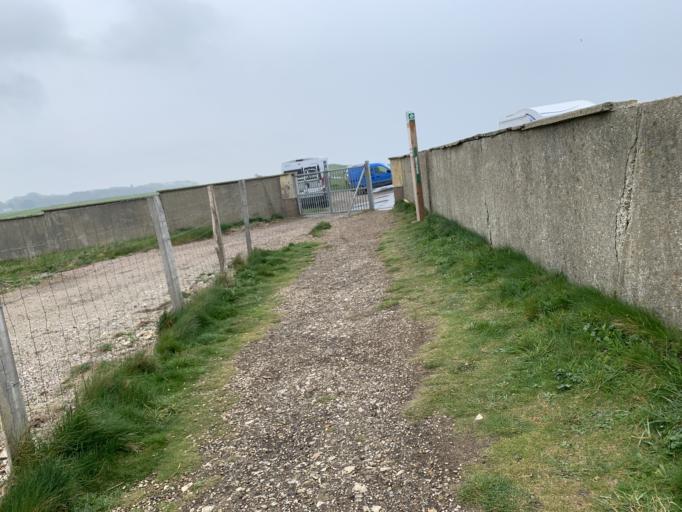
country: FR
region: Haute-Normandie
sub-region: Departement de la Seine-Maritime
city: Saint-Jouin-Bruneval
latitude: 49.6833
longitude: 0.1650
